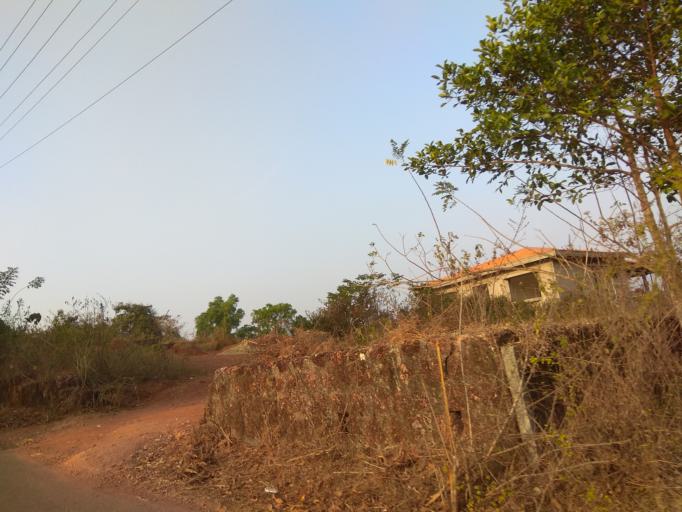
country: IN
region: Karnataka
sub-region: Dakshina Kannada
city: Mangalore
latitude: 12.9139
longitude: 74.8599
